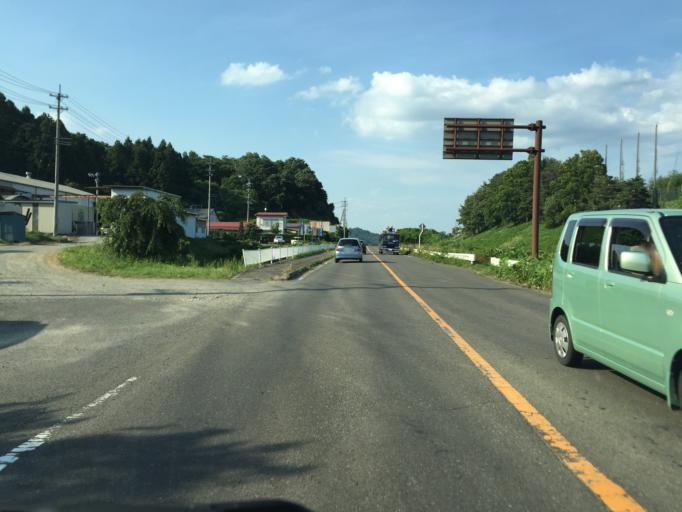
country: JP
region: Fukushima
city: Nihommatsu
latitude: 37.5716
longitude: 140.4153
